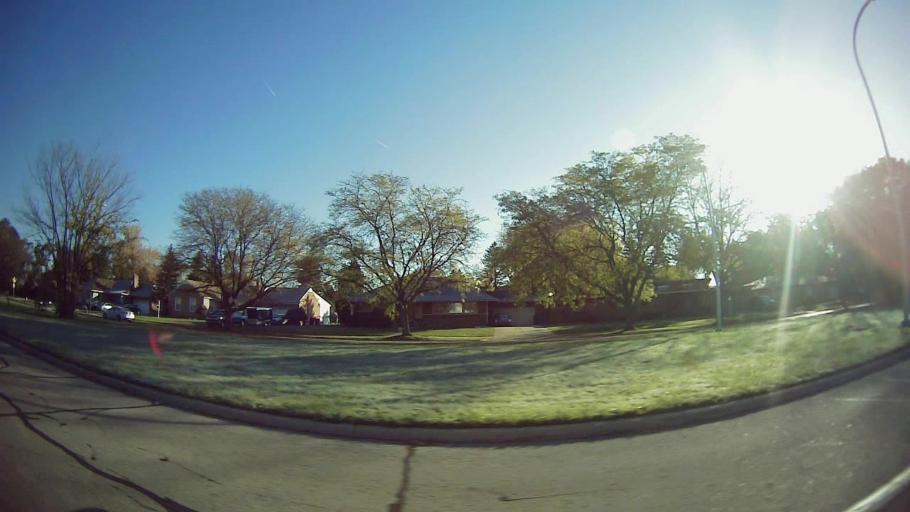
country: US
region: Michigan
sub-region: Wayne County
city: Dearborn
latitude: 42.3546
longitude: -83.1701
